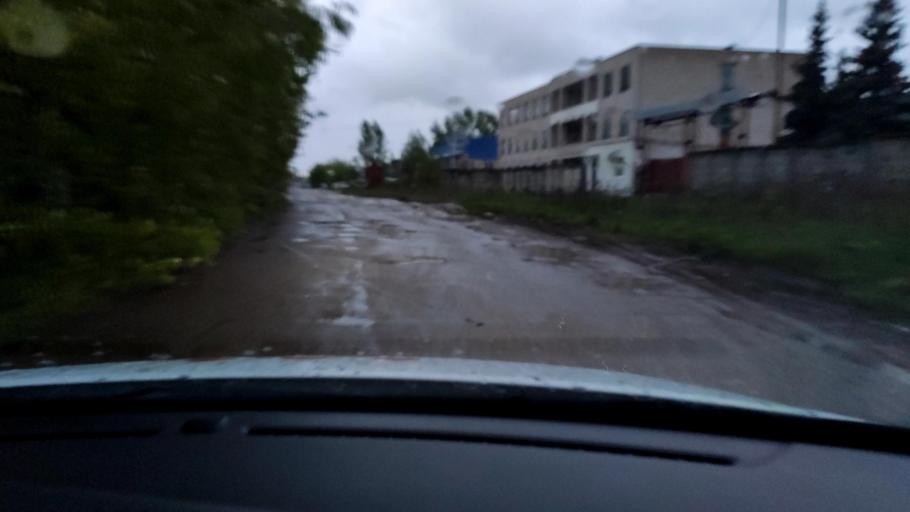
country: RU
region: Tatarstan
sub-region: Gorod Kazan'
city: Kazan
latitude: 55.7217
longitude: 49.1236
